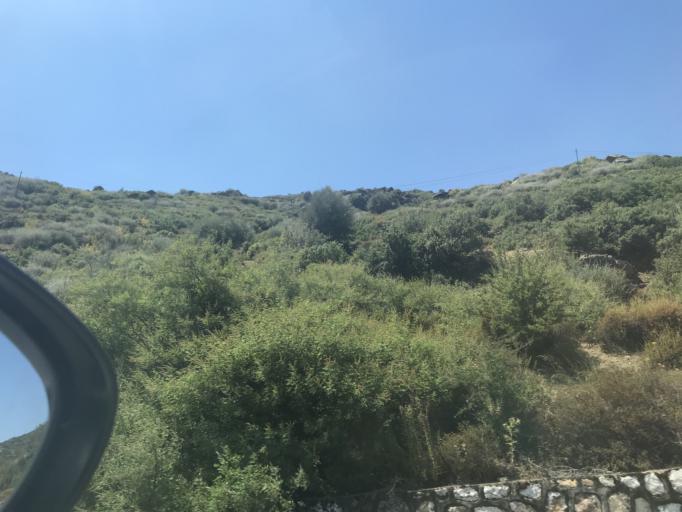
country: TR
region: Aydin
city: Akcaova
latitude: 37.5111
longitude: 28.0983
